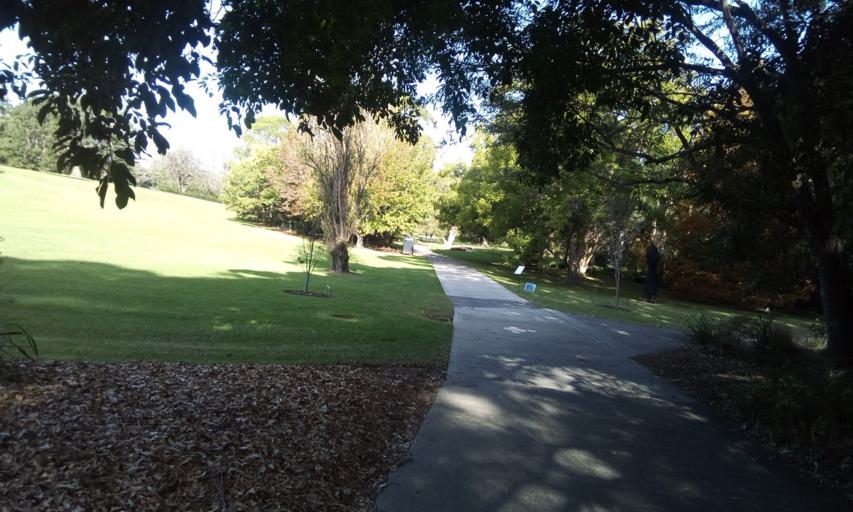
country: AU
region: New South Wales
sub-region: Wollongong
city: Mount Ousley
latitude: -34.4090
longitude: 150.8759
